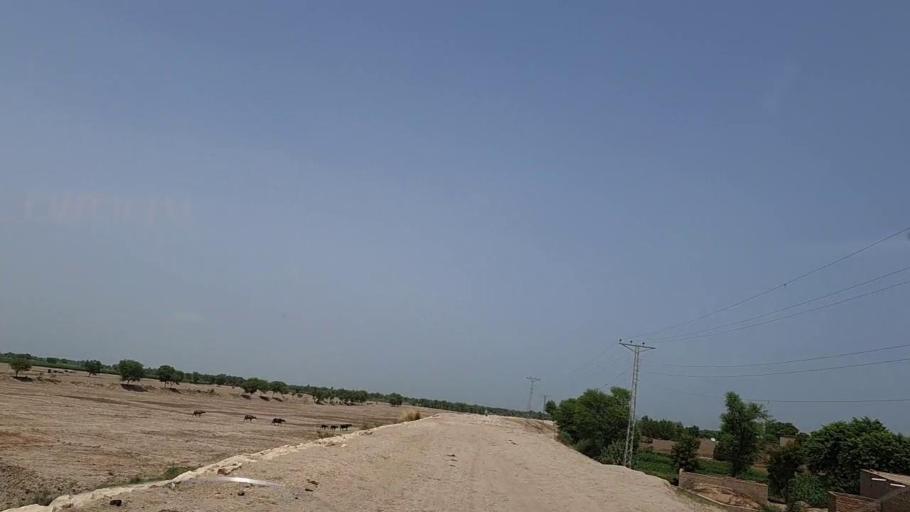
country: PK
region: Sindh
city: Tharu Shah
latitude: 27.0162
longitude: 68.1038
